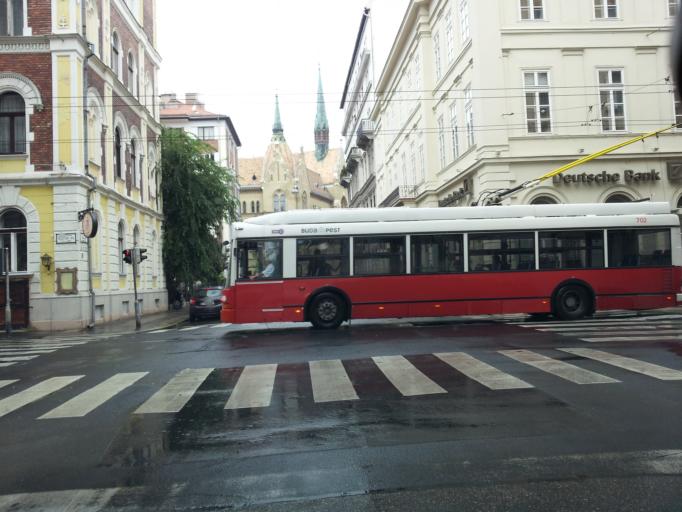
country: HU
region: Budapest
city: Budapest VI. keruelet
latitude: 47.5067
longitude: 19.0521
